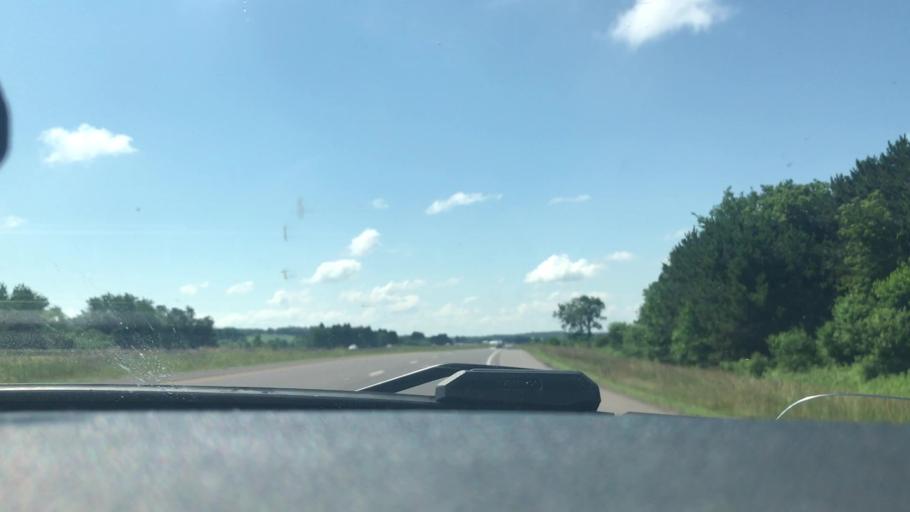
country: US
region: Wisconsin
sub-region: Chippewa County
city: Bloomer
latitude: 45.0625
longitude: -91.4667
